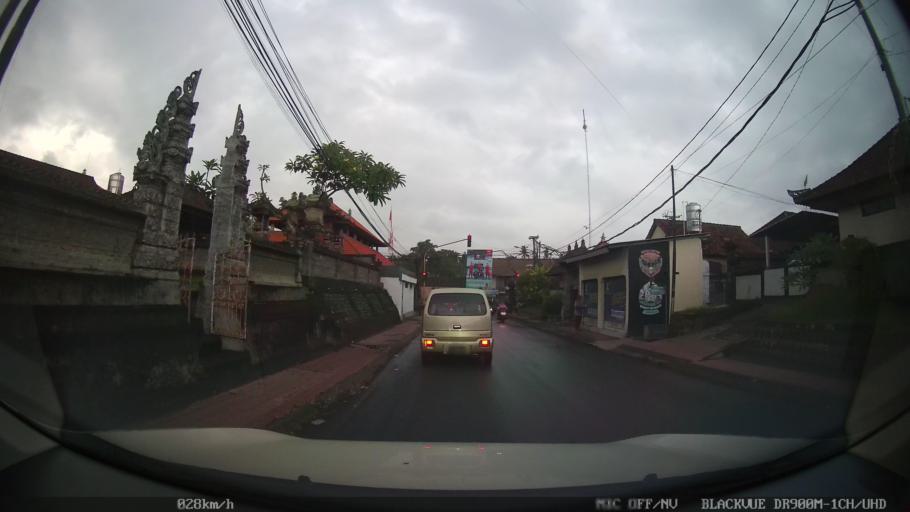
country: ID
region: Bali
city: Banjar Pasekan
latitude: -8.6035
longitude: 115.2809
